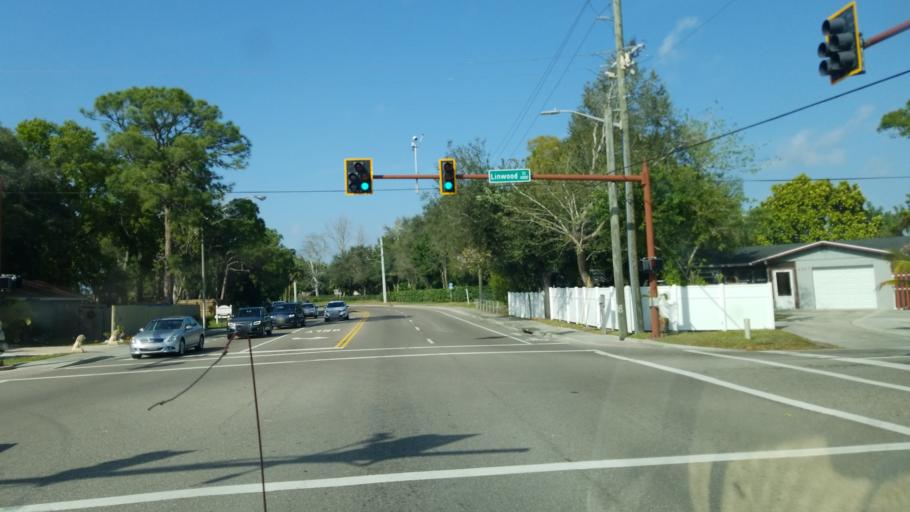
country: US
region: Florida
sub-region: Sarasota County
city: Sarasota Springs
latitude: 27.3150
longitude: -82.4822
